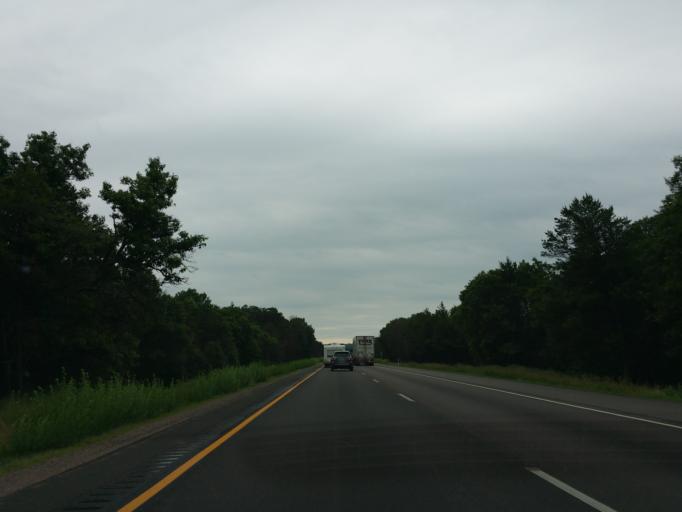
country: US
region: Wisconsin
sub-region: Trempealeau County
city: Osseo
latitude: 44.5535
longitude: -91.1718
